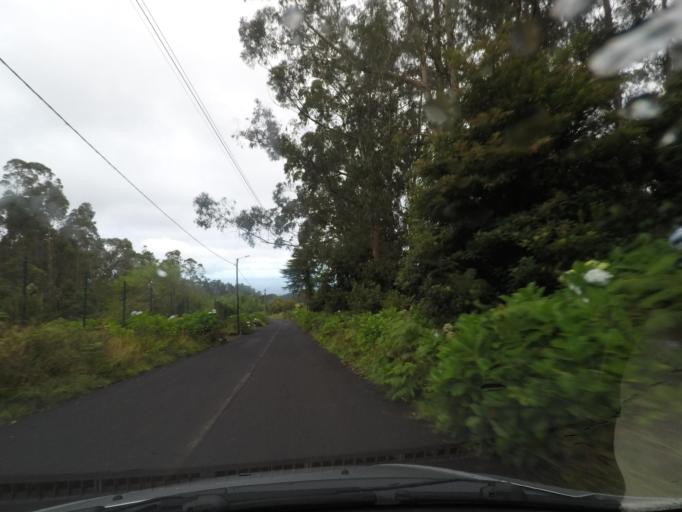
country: PT
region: Madeira
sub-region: Santana
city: Santana
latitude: 32.7837
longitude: -16.8938
